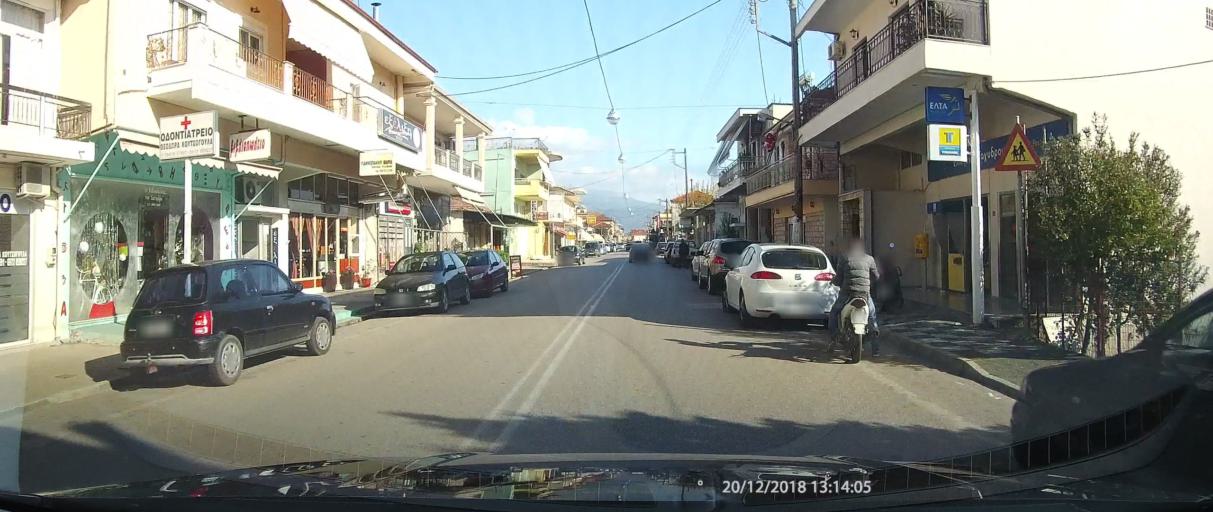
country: GR
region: West Greece
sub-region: Nomos Aitolias kai Akarnanias
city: Kainouryion
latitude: 38.6043
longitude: 21.4851
